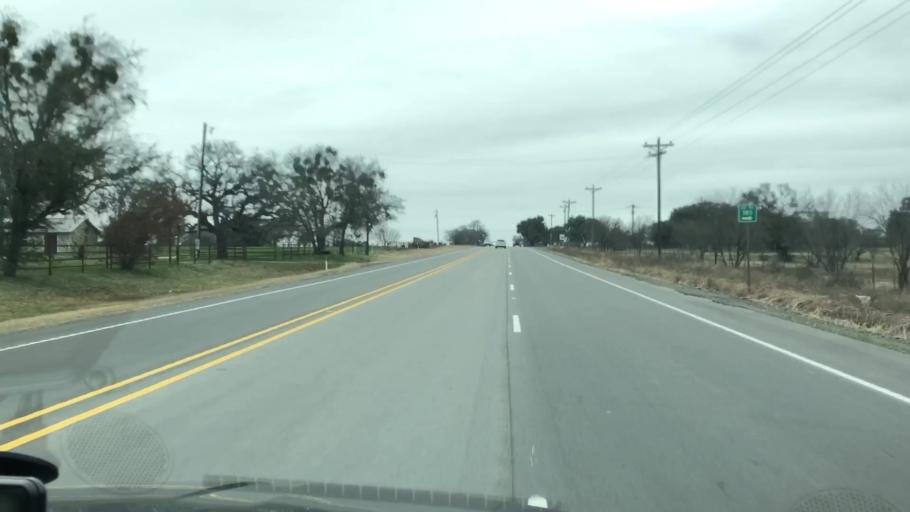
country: US
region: Texas
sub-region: Erath County
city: Stephenville
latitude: 32.1542
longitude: -98.1450
